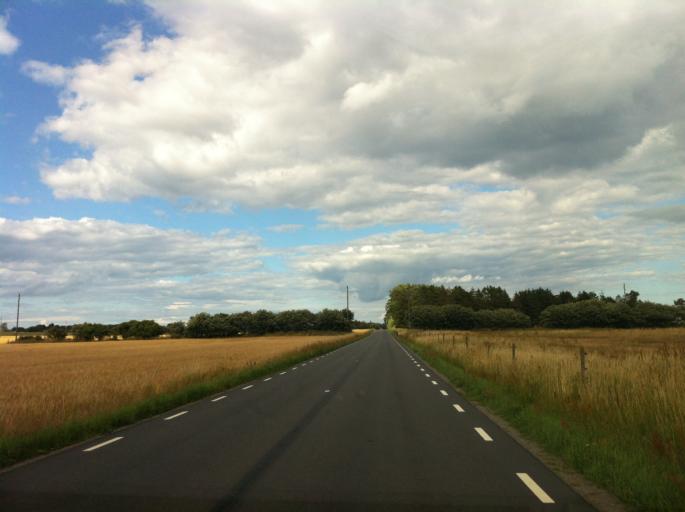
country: SE
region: Skane
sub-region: Simrishamns Kommun
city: Simrishamn
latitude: 55.4309
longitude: 14.2231
